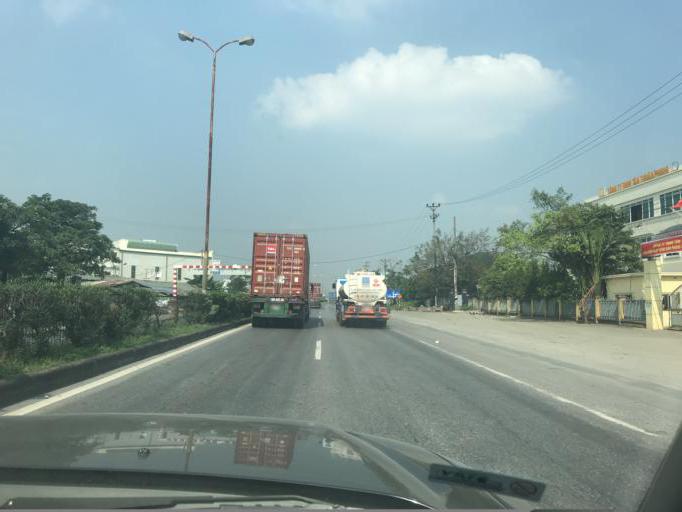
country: VN
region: Hai Phong
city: An Duong
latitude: 20.8779
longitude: 106.6126
